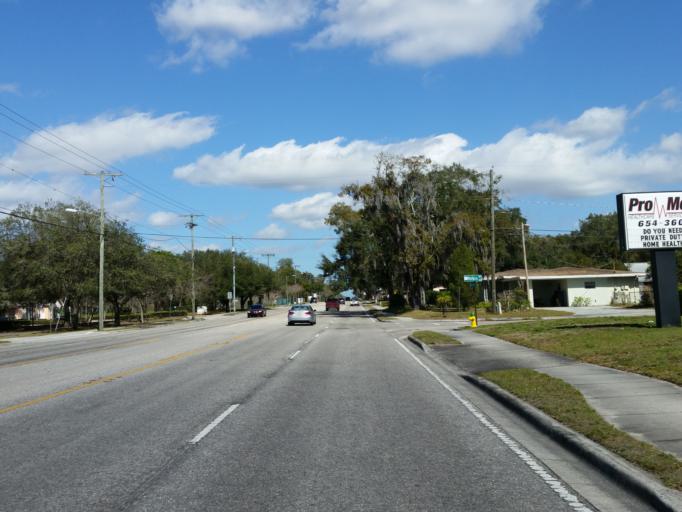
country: US
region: Florida
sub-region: Hillsborough County
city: Brandon
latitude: 27.9508
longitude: -82.2858
